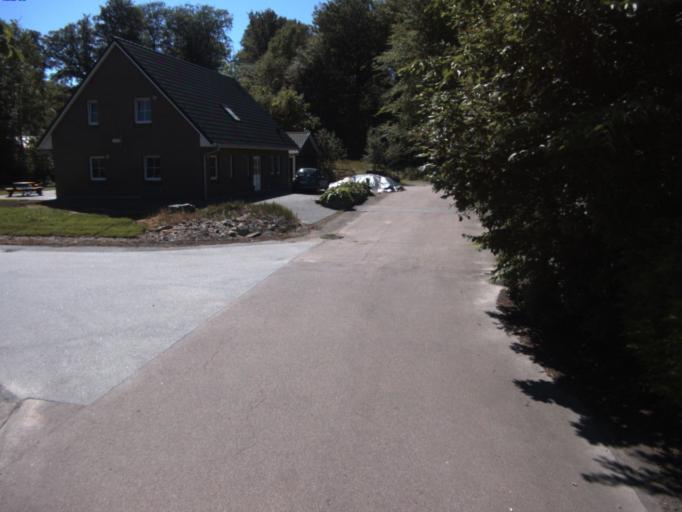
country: SE
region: Skane
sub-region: Helsingborg
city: Morarp
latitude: 56.0575
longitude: 12.8703
